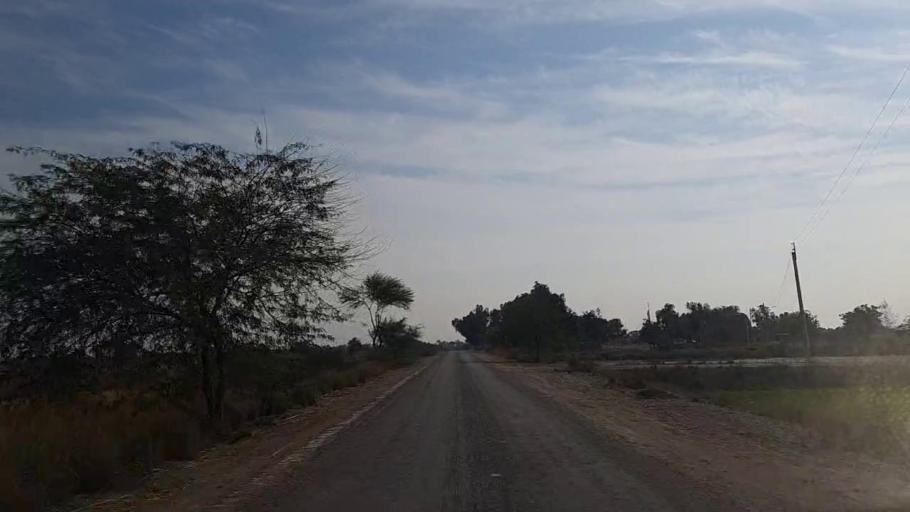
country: PK
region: Sindh
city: Daur
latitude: 26.4729
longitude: 68.4179
